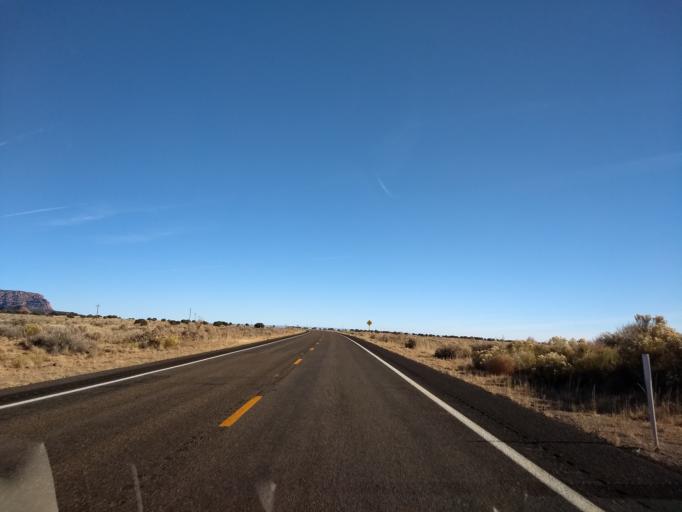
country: US
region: Arizona
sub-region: Mohave County
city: Colorado City
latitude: 36.8856
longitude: -112.9048
